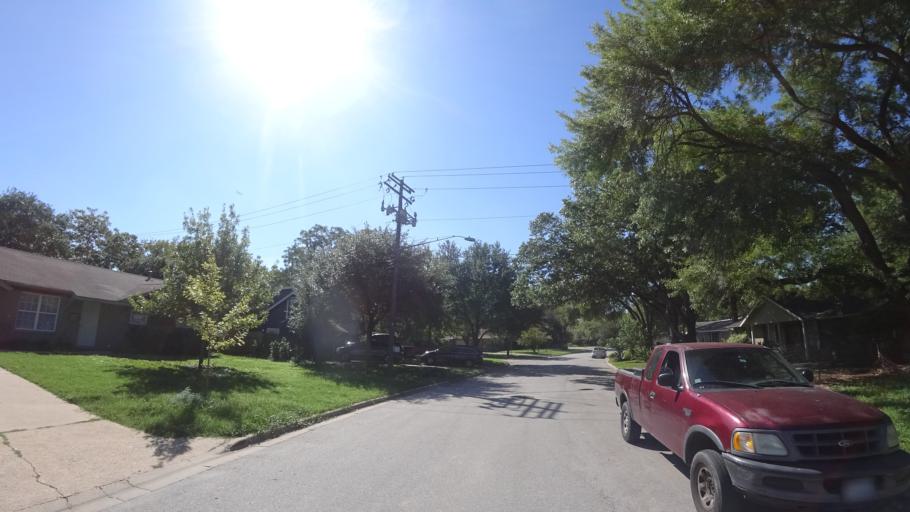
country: US
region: Texas
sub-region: Travis County
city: Austin
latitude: 30.3197
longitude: -97.6935
